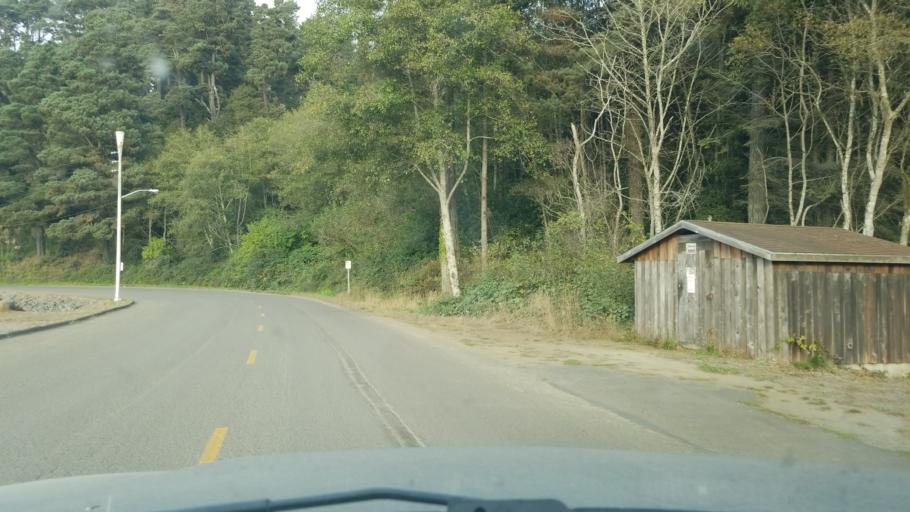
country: US
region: California
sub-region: Mendocino County
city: Fort Bragg
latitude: 39.4225
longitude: -123.8013
